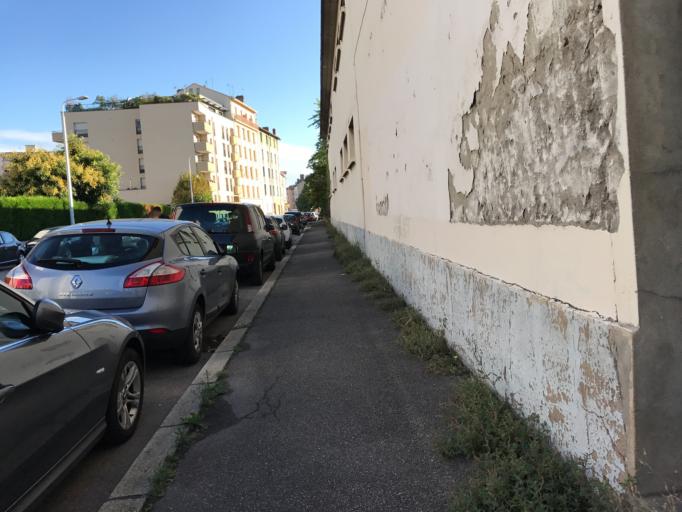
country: FR
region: Rhone-Alpes
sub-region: Departement du Rhone
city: Lyon
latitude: 45.7313
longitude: 4.8386
